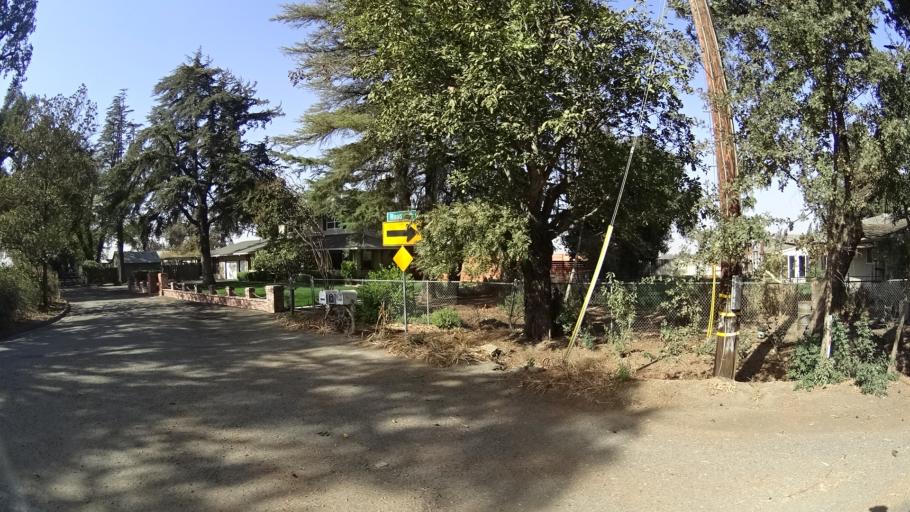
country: US
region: California
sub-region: Yolo County
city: Woodland
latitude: 38.7425
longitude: -121.8033
